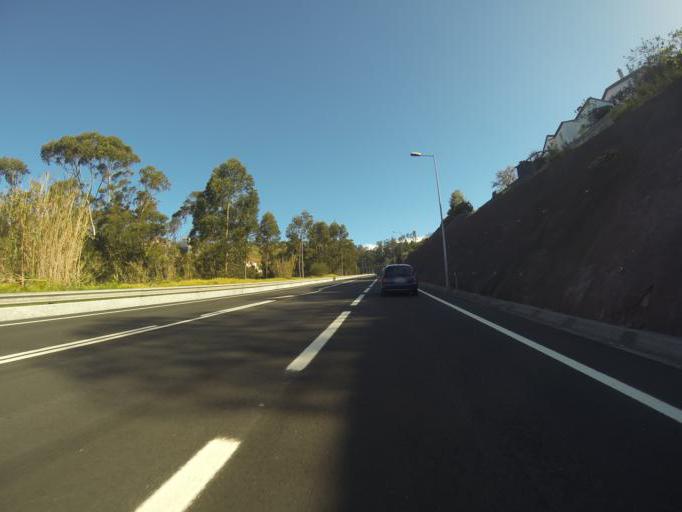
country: PT
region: Madeira
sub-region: Calheta
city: Estreito da Calheta
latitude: 32.7419
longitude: -17.1947
